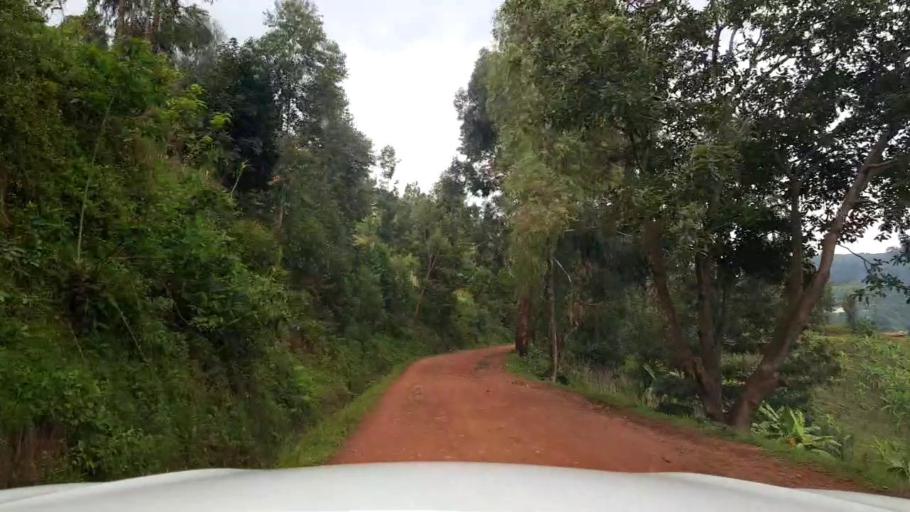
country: UG
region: Western Region
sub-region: Kisoro District
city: Kisoro
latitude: -1.3896
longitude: 29.7975
